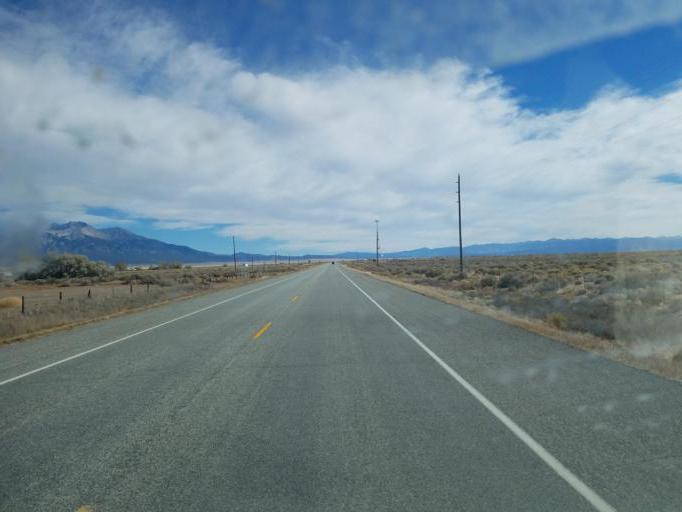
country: US
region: Colorado
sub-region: Alamosa County
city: Alamosa East
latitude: 37.4744
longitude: -105.7320
